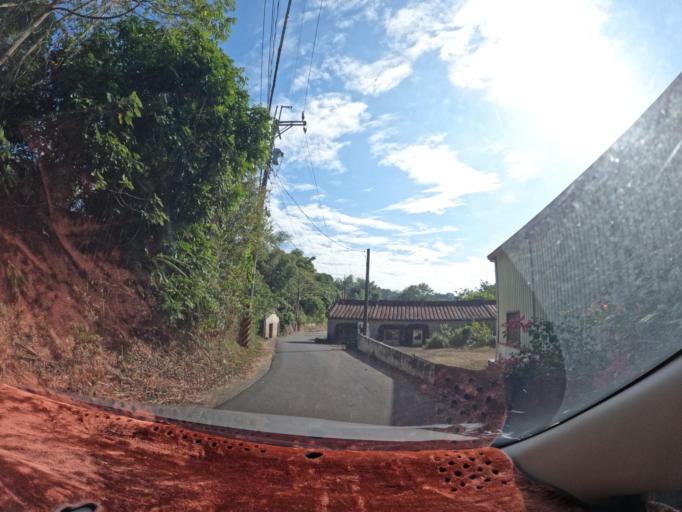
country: TW
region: Taiwan
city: Yujing
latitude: 23.0141
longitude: 120.3855
